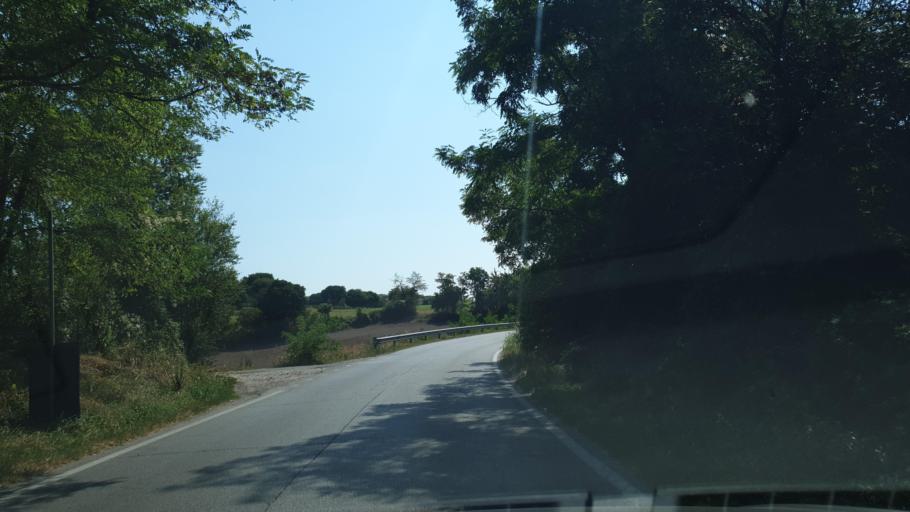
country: IT
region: Lombardy
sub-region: Provincia di Brescia
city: Lonato
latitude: 45.4756
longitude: 10.4778
